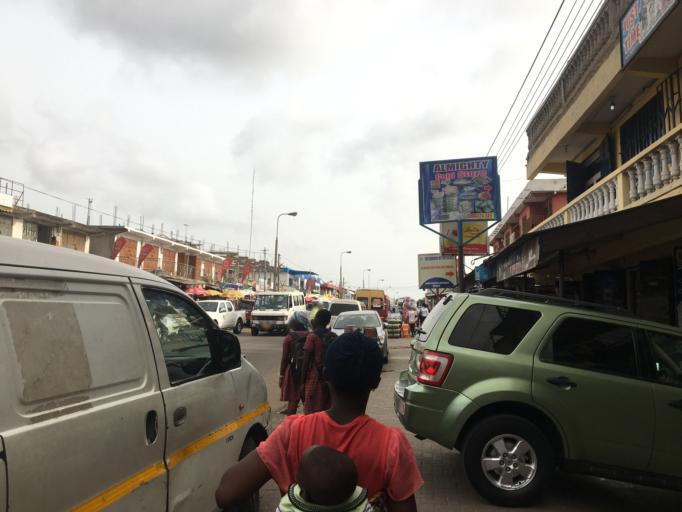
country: GH
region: Greater Accra
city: Accra
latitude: 5.5853
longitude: -0.1975
